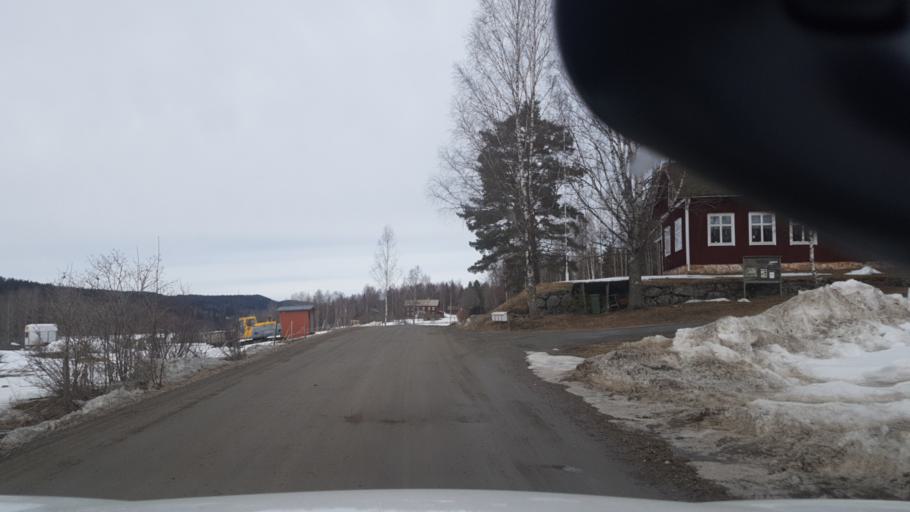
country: SE
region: Vaermland
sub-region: Eda Kommun
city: Amotfors
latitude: 59.7671
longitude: 12.4444
